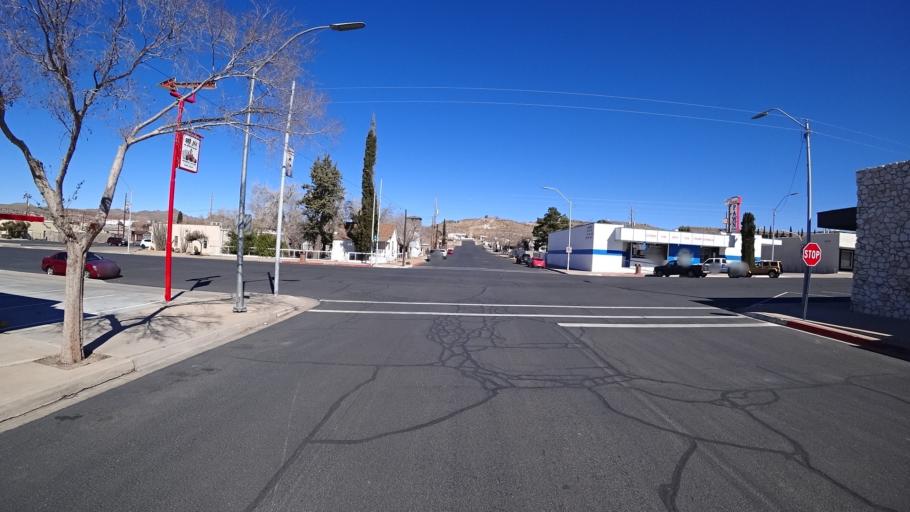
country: US
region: Arizona
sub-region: Mohave County
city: Kingman
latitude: 35.1897
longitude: -114.0562
